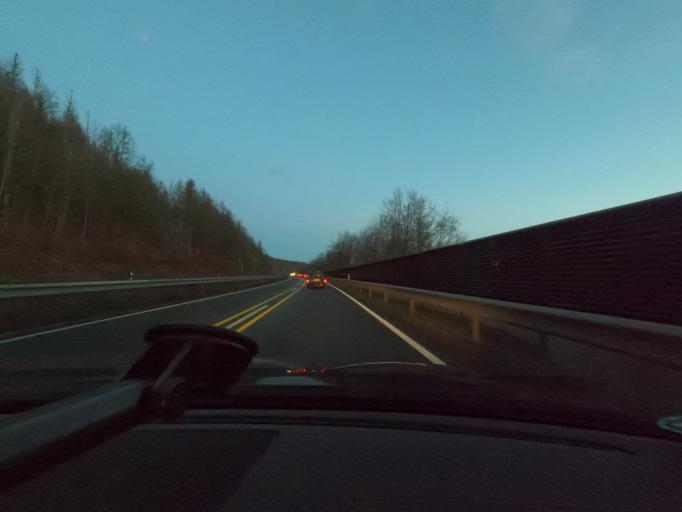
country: DE
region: Lower Saxony
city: Herzberg am Harz
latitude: 51.6322
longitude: 10.3709
